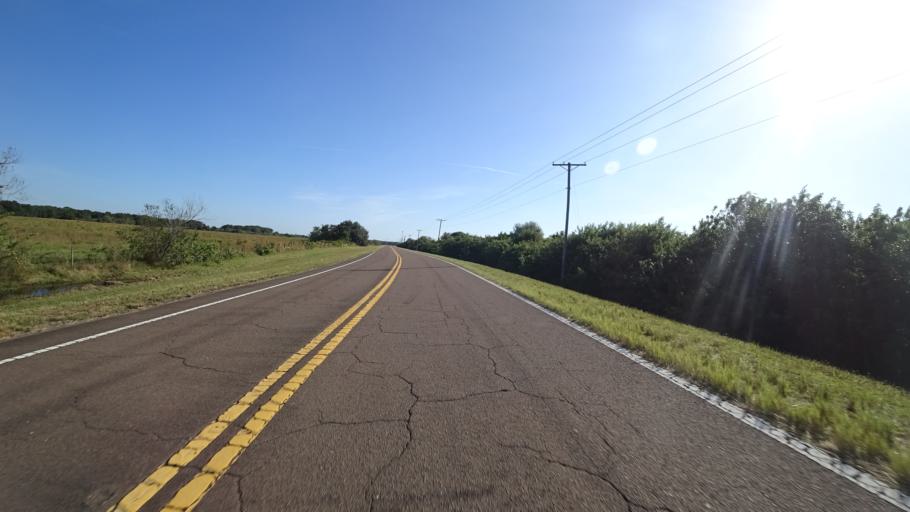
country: US
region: Florida
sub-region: Hillsborough County
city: Ruskin
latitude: 27.6541
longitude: -82.4496
